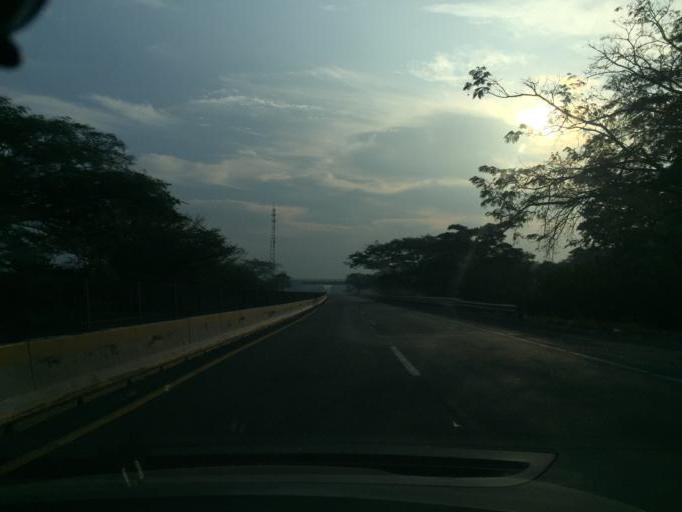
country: MX
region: Veracruz
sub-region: Omealca
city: Mata Tenatito (Casco Hacienda)
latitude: 18.7891
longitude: -96.5613
